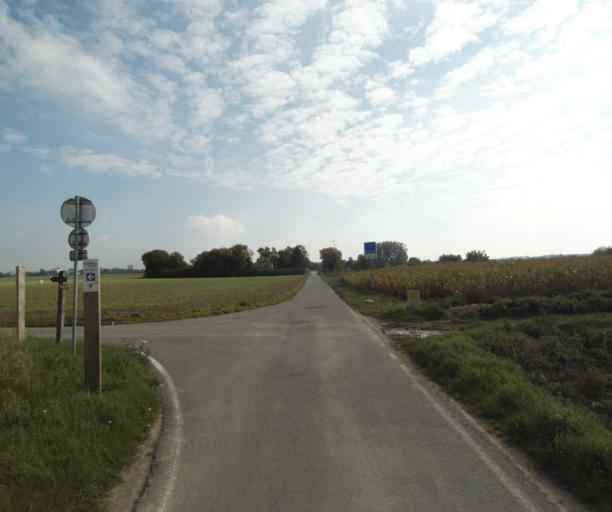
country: FR
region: Nord-Pas-de-Calais
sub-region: Departement du Nord
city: Emmerin
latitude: 50.5830
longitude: 3.0157
